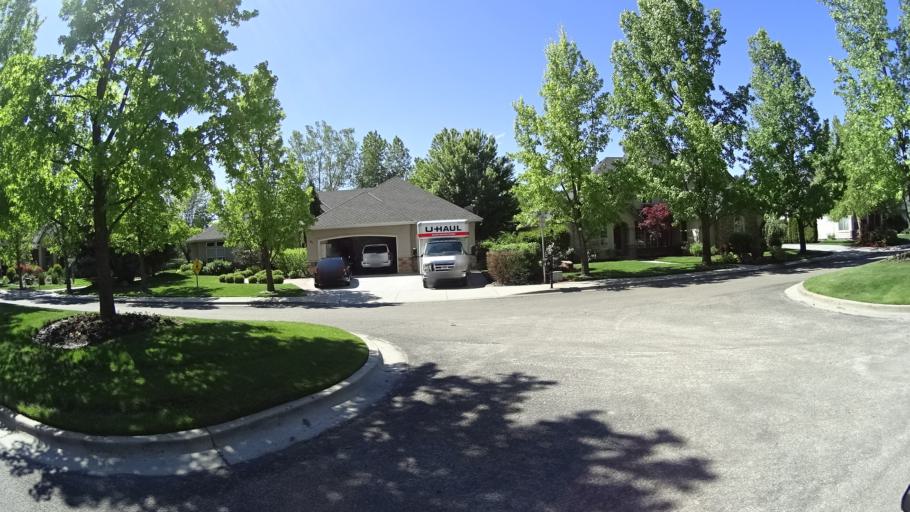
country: US
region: Idaho
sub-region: Ada County
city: Eagle
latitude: 43.6691
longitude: -116.3558
